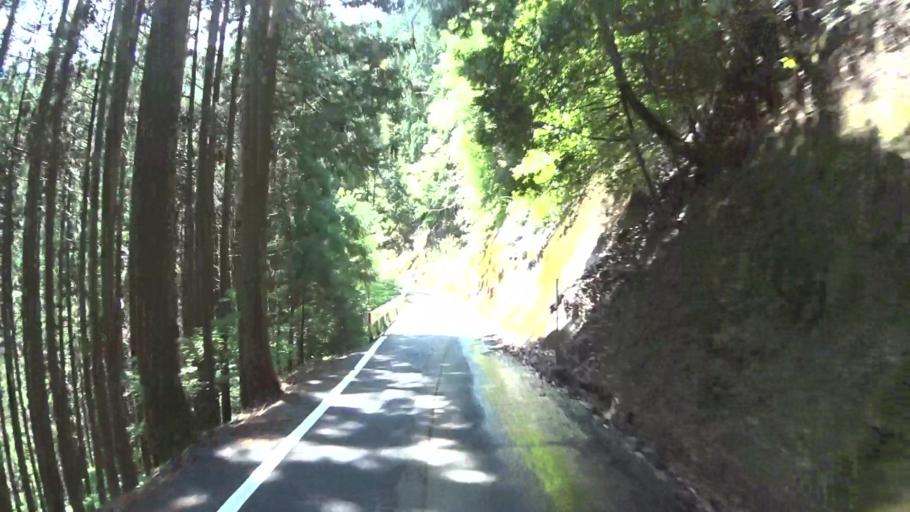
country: JP
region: Kyoto
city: Kameoka
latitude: 35.1271
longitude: 135.5824
